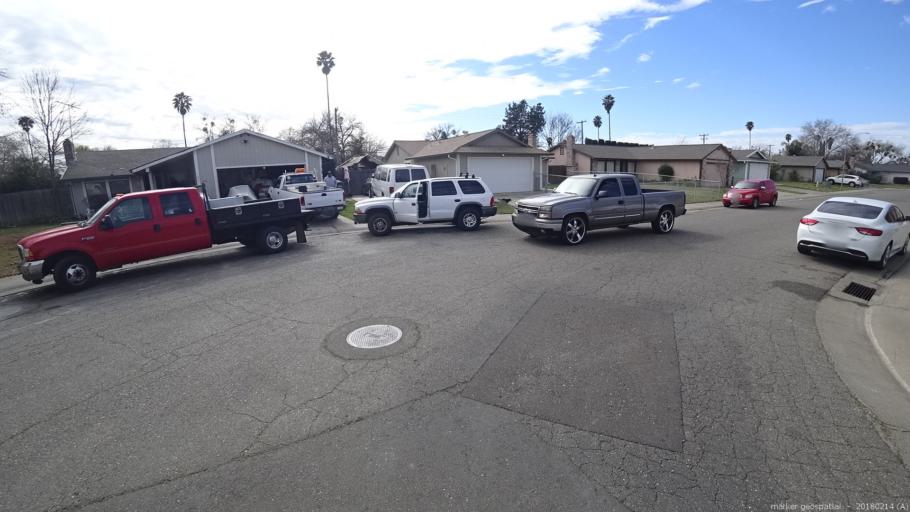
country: US
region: California
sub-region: Sacramento County
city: Rio Linda
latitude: 38.6871
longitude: -121.4625
